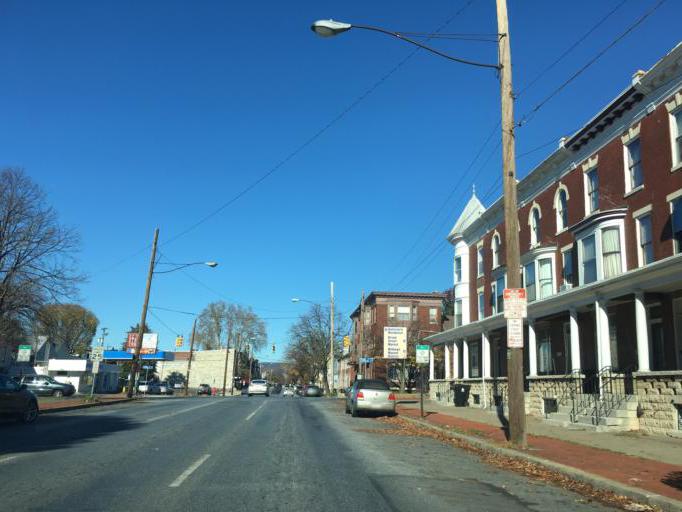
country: US
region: Pennsylvania
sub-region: Dauphin County
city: Harrisburg
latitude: 40.2680
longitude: -76.8911
